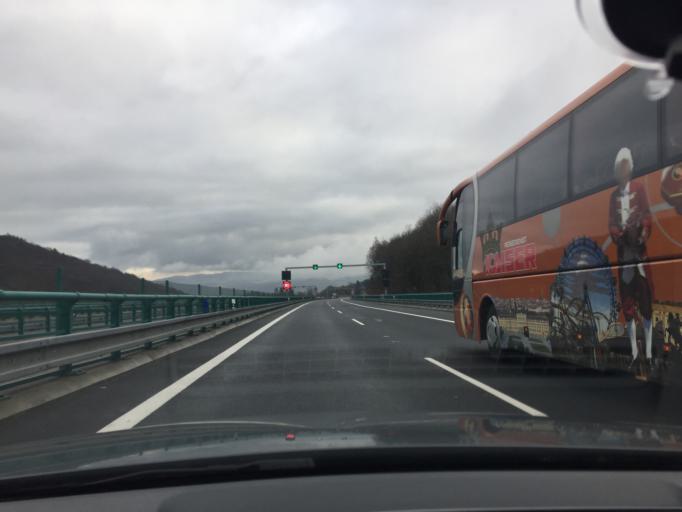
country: CZ
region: Ustecky
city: Libouchec
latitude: 50.7513
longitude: 13.9941
